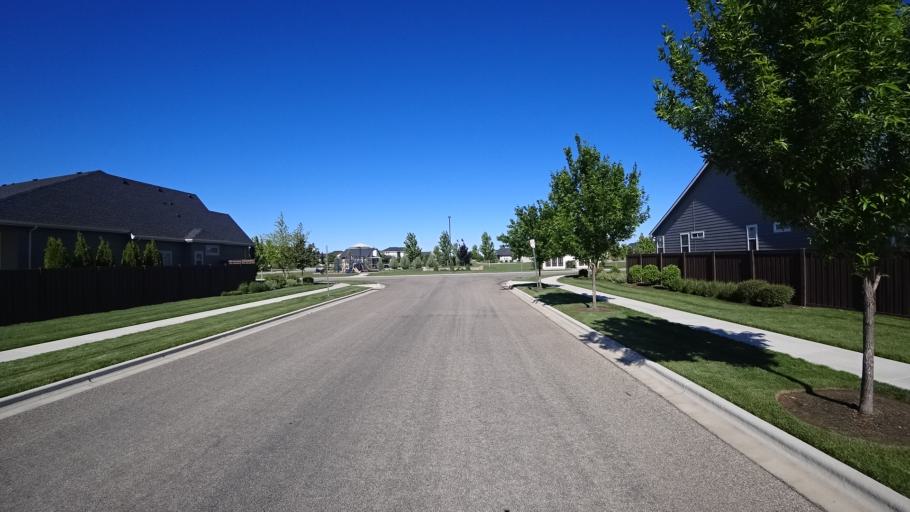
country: US
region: Idaho
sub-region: Ada County
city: Star
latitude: 43.6575
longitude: -116.4449
